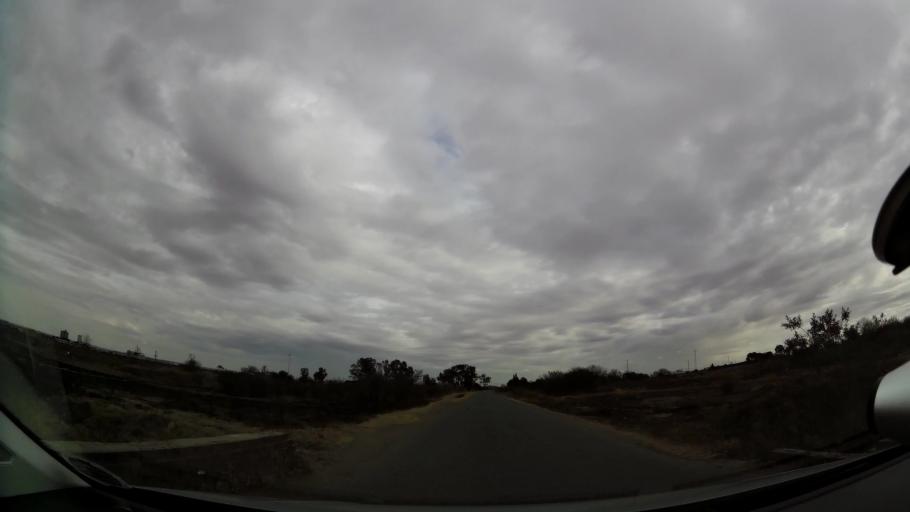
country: ZA
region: Orange Free State
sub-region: Fezile Dabi District Municipality
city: Kroonstad
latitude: -27.6505
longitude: 27.2147
